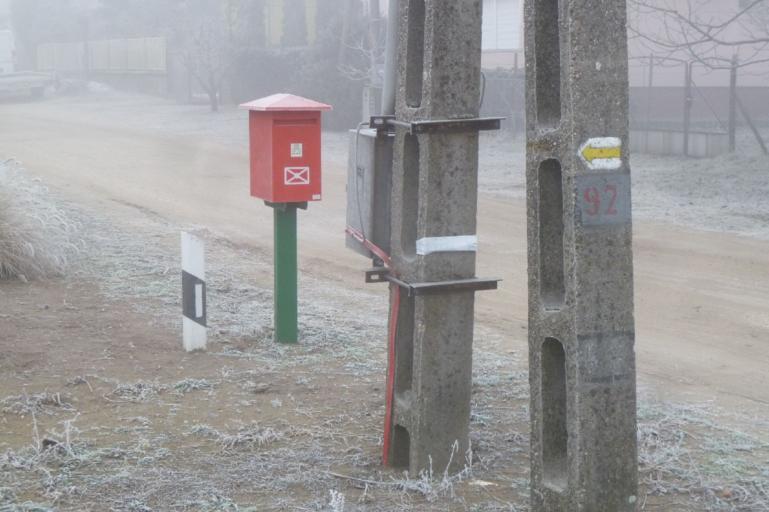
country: HU
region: Pest
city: Tapioszele
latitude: 47.3196
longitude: 19.8778
